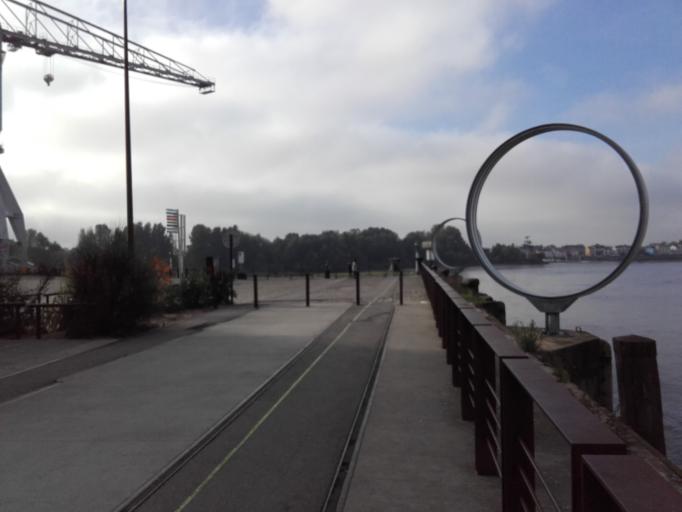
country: FR
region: Pays de la Loire
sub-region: Departement de la Loire-Atlantique
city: Nantes
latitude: 47.2002
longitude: -1.5742
